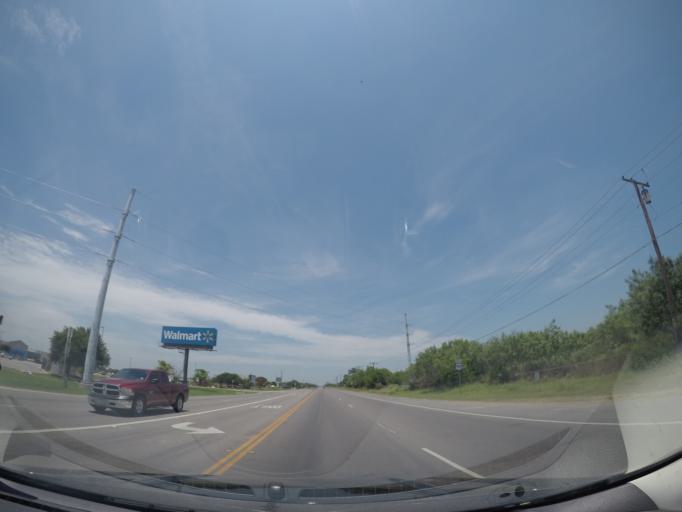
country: US
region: Texas
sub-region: Uvalde County
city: Uvalde
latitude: 29.2330
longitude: -99.7529
